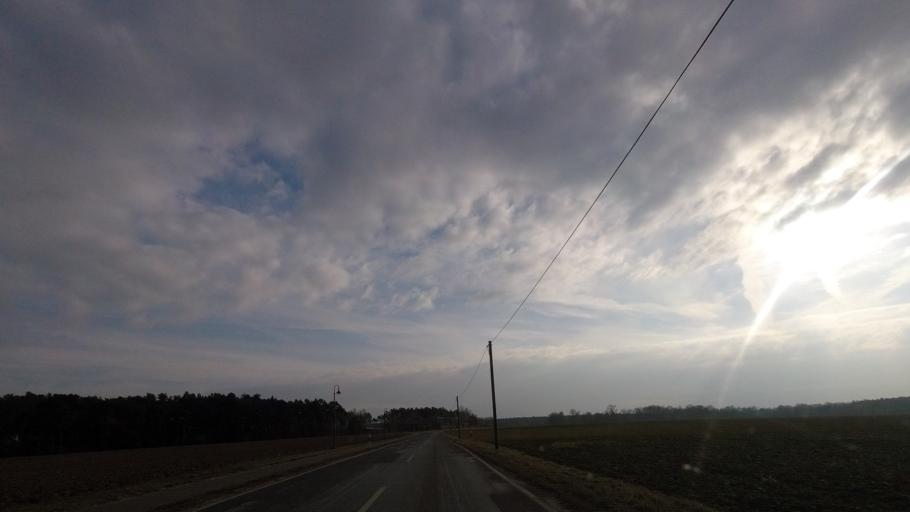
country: DE
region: Brandenburg
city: Belzig
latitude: 52.1687
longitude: 12.6799
